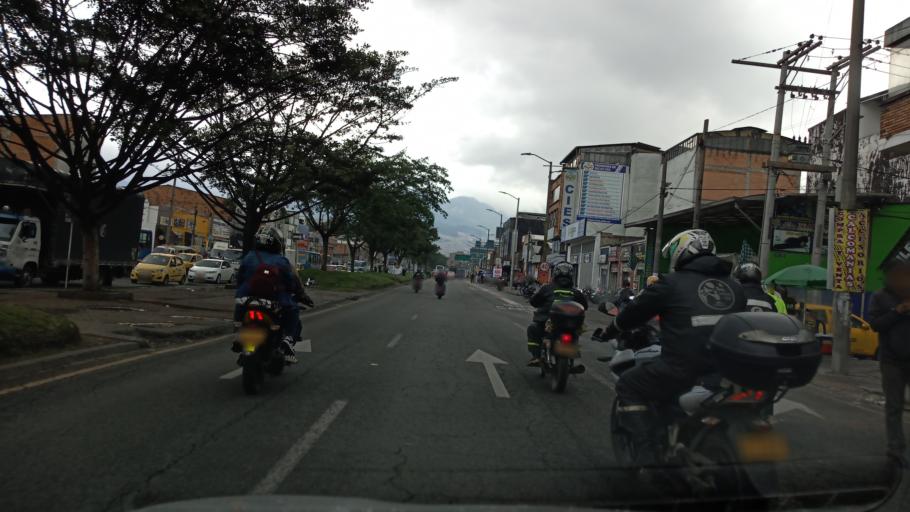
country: CO
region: Bogota D.C.
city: Bogota
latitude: 4.5917
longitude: -74.1109
